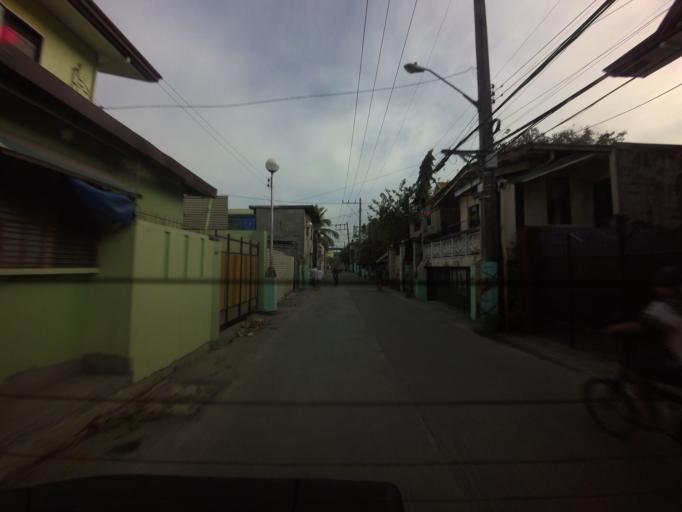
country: PH
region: Central Luzon
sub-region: Province of Bulacan
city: Obando
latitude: 14.7099
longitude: 120.9446
